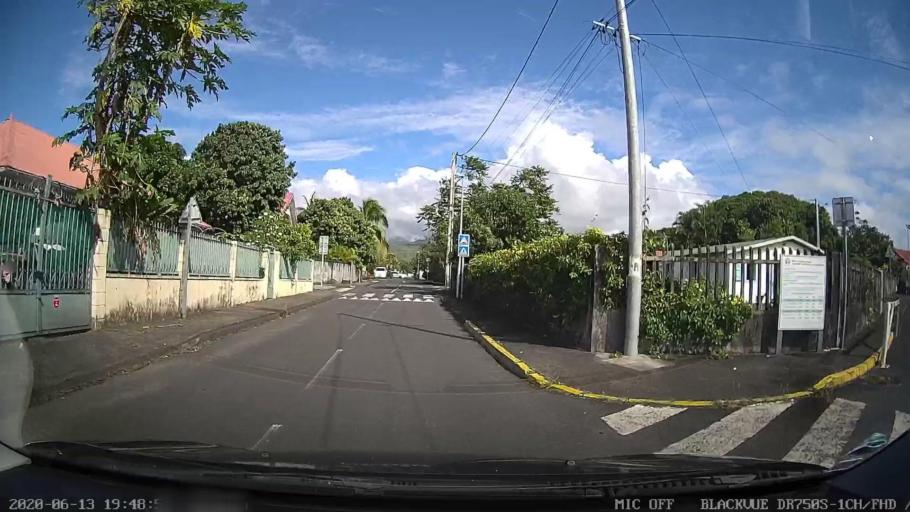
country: RE
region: Reunion
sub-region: Reunion
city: Bras-Panon
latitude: -21.0032
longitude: 55.6909
